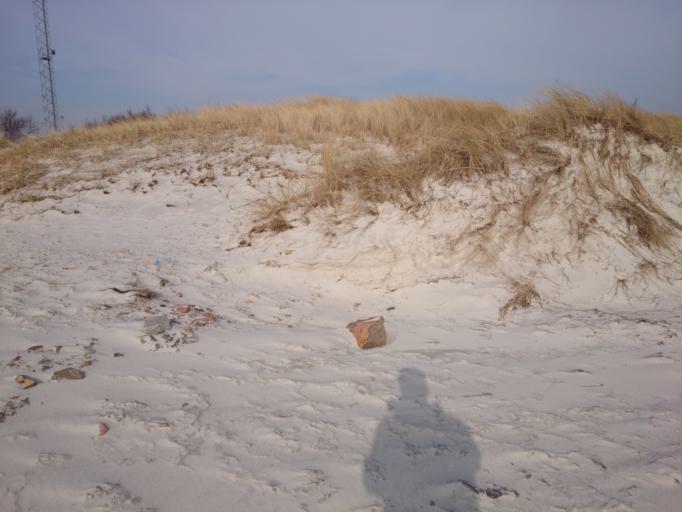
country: SE
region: Skane
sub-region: Vellinge Kommun
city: Skanor med Falsterbo
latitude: 55.3923
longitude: 12.8594
